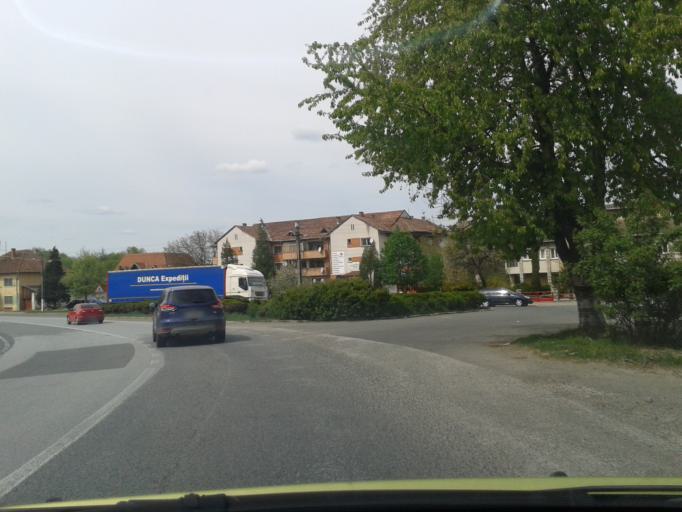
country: RO
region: Hunedoara
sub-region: Comuna Dobra
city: Dobra
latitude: 45.9128
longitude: 22.5713
